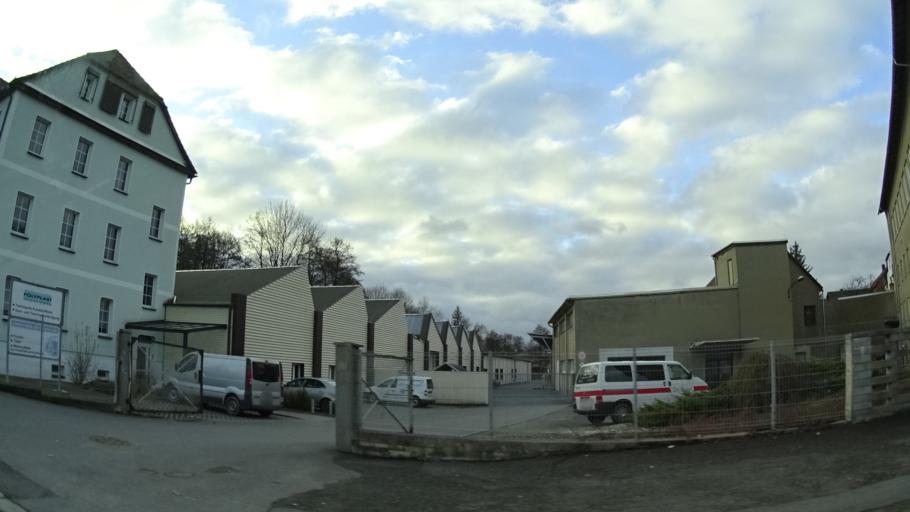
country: DE
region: Thuringia
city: Auma
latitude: 50.7032
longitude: 11.8966
